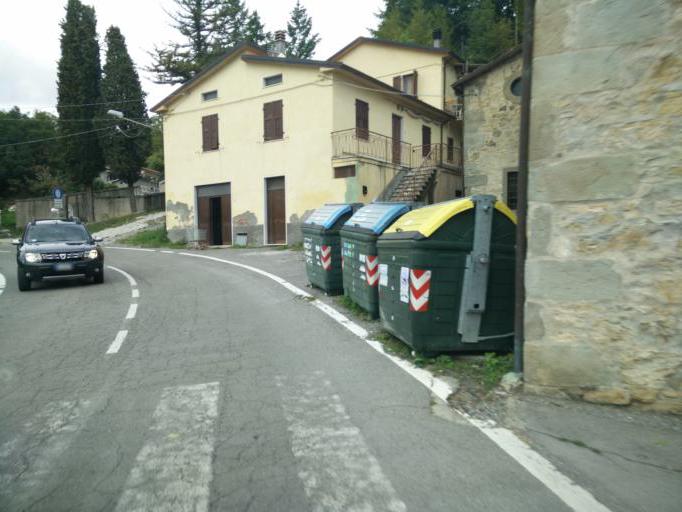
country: IT
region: Tuscany
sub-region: Provincia di Massa-Carrara
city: Casola in Lunigiana
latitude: 44.2072
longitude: 10.1988
